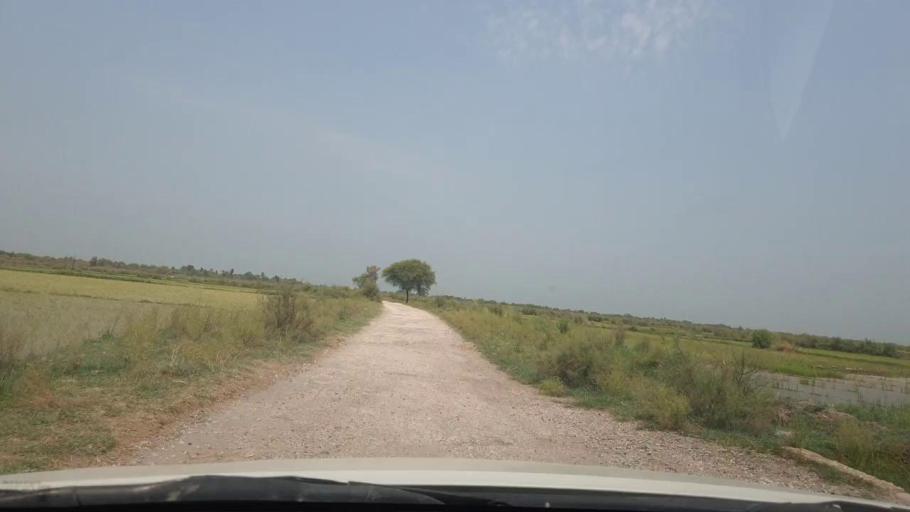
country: PK
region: Sindh
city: Rustam jo Goth
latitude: 28.0521
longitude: 68.7514
